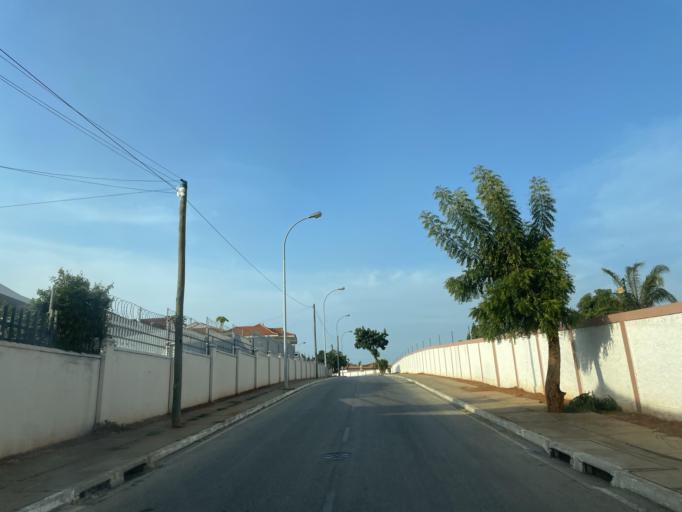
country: AO
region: Luanda
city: Luanda
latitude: -8.9289
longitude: 13.1801
